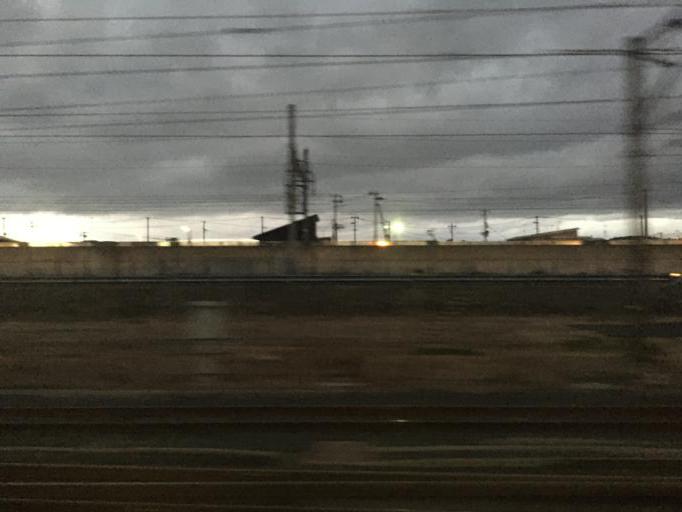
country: JP
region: Aomori
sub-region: Hachinohe Shi
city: Uchimaru
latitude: 40.5122
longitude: 141.4343
